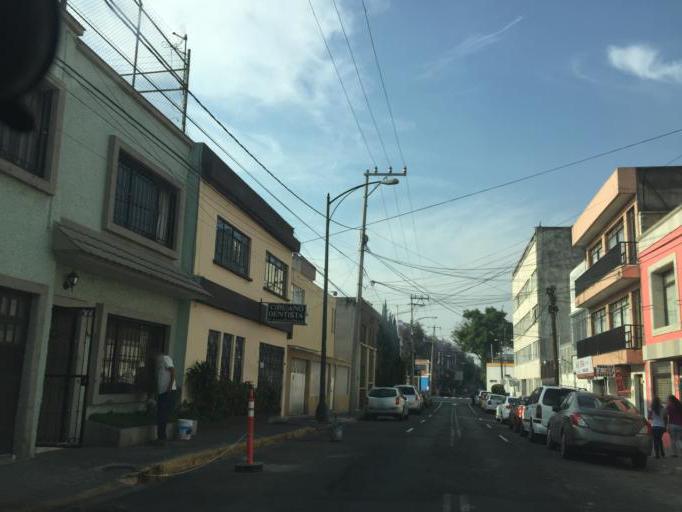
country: MX
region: Mexico
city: Colonia Lindavista
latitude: 19.4894
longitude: -99.1359
